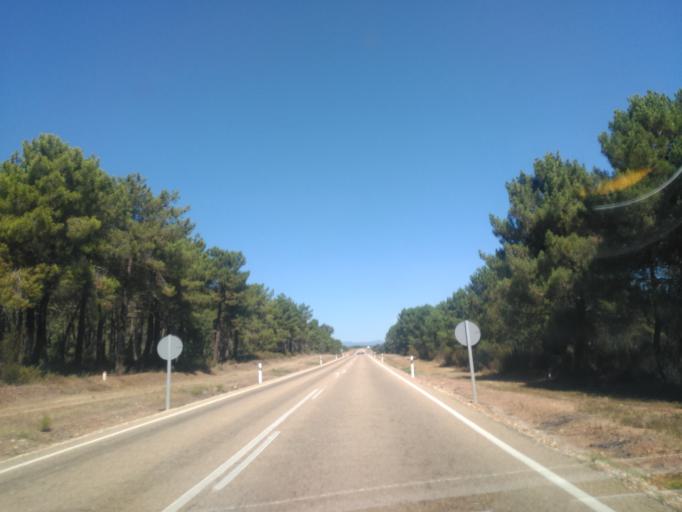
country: ES
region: Castille and Leon
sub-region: Provincia de Zamora
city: Tabara
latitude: 41.8680
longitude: -6.0041
